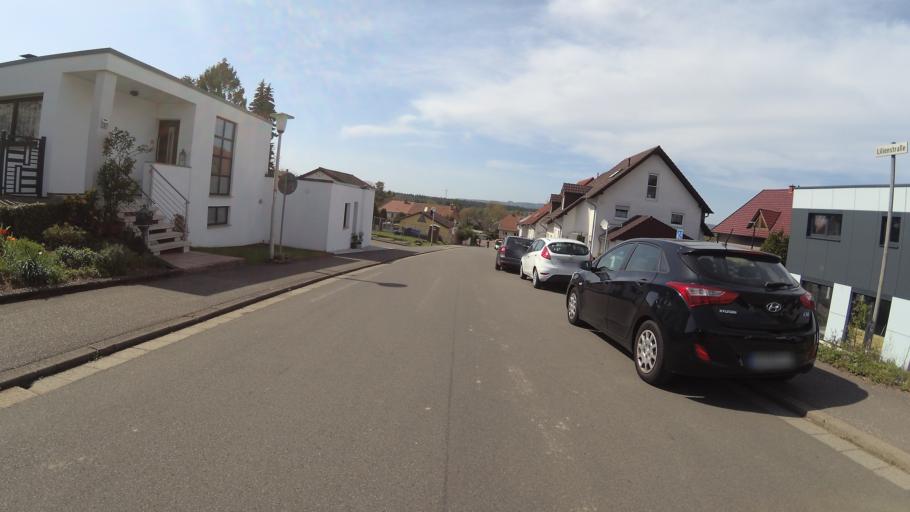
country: DE
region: Saarland
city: Homburg
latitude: 49.3470
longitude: 7.3659
